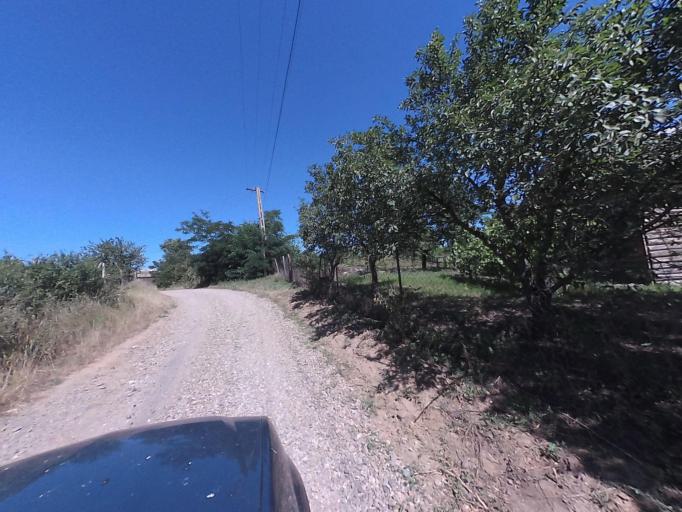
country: RO
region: Vaslui
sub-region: Comuna Costesti
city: Costesti
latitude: 46.4778
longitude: 27.7940
